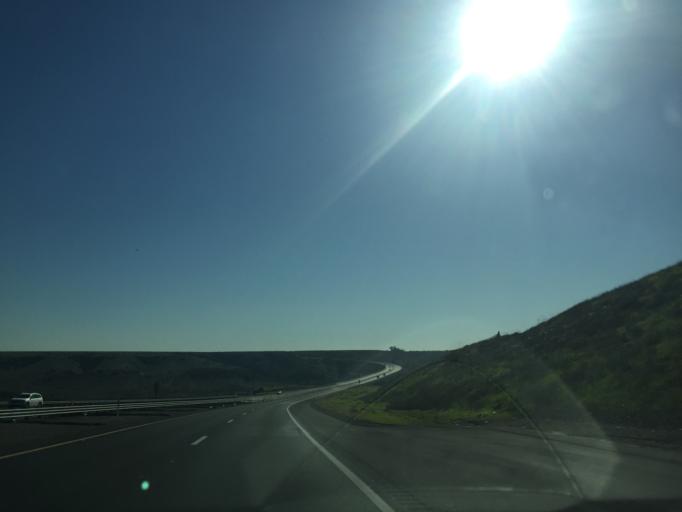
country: US
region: California
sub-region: San Diego County
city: Bonita
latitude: 32.5999
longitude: -116.9643
